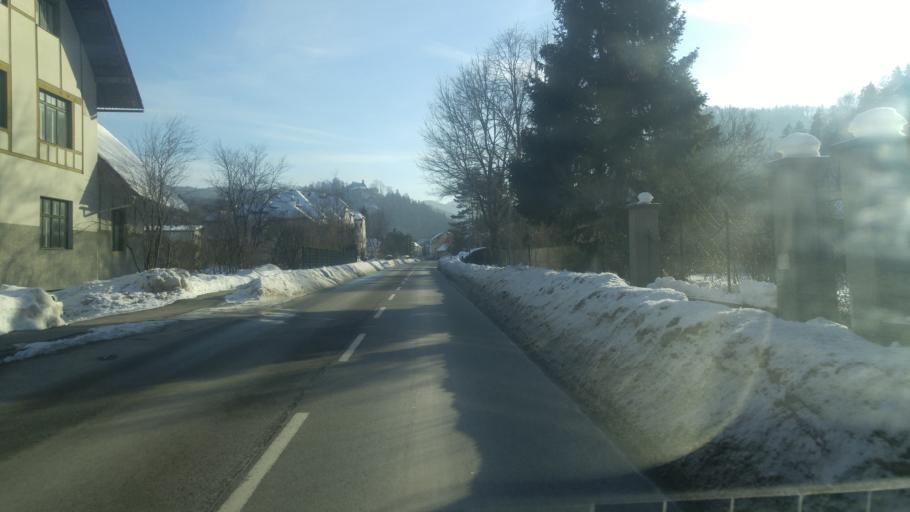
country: AT
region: Lower Austria
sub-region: Politischer Bezirk Lilienfeld
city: Hohenberg
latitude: 47.9130
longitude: 15.6180
